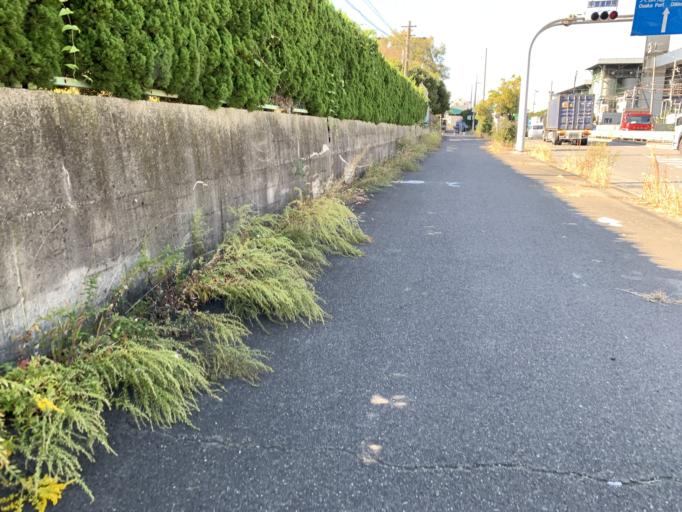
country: JP
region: Osaka
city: Sakai
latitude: 34.6499
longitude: 135.4428
